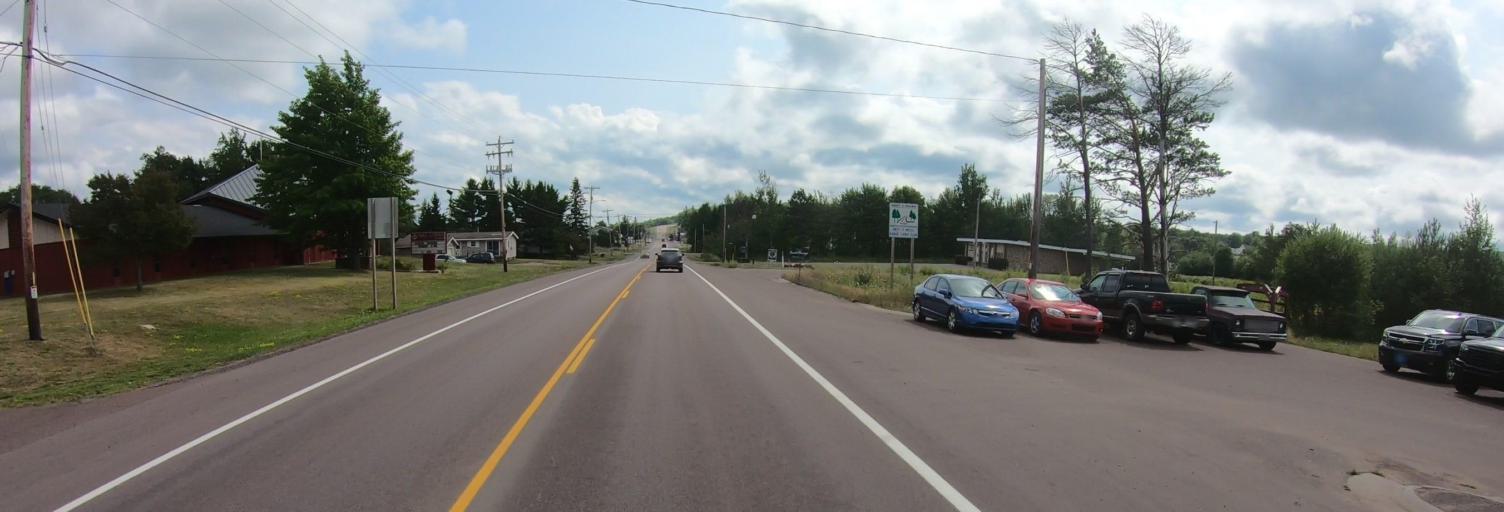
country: US
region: Michigan
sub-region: Houghton County
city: Hancock
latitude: 47.0762
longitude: -88.6405
